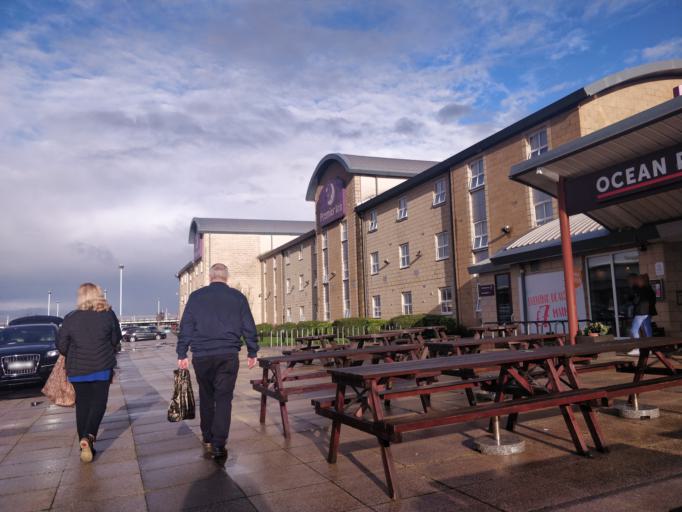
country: GB
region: England
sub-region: Sefton
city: Southport
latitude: 53.6512
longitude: -3.0146
